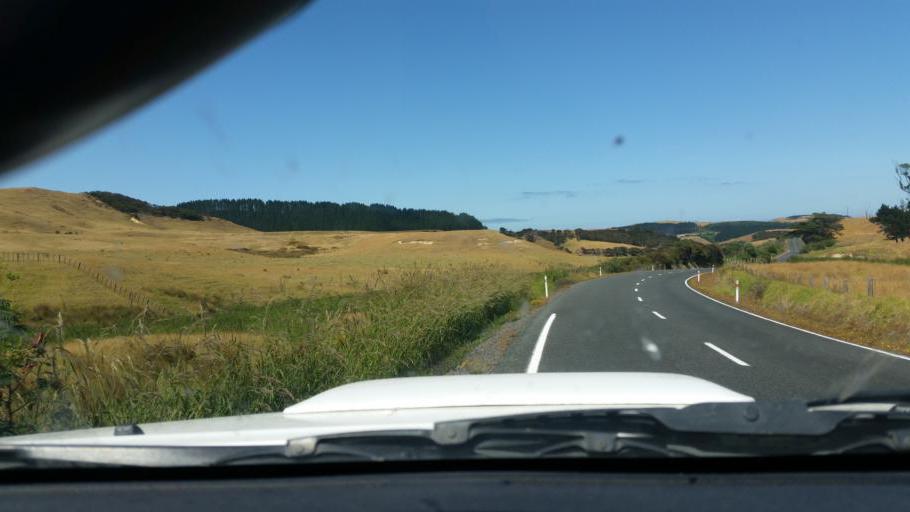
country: NZ
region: Northland
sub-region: Kaipara District
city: Dargaville
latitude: -35.8242
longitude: 173.6793
